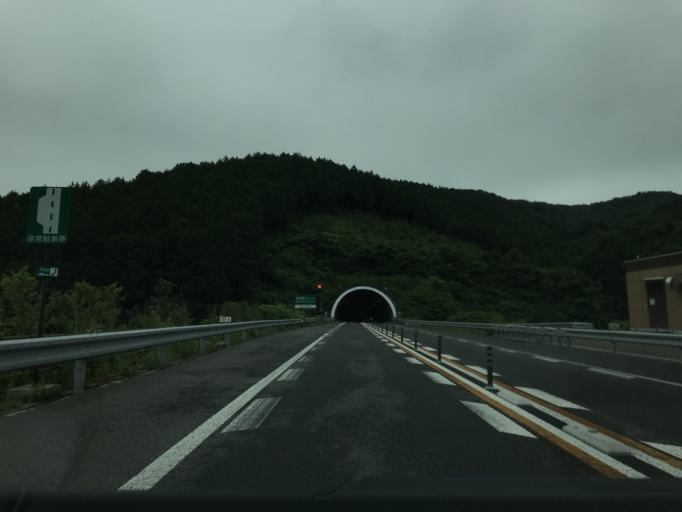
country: JP
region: Fukuoka
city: Nakatsu
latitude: 33.5122
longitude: 131.2837
